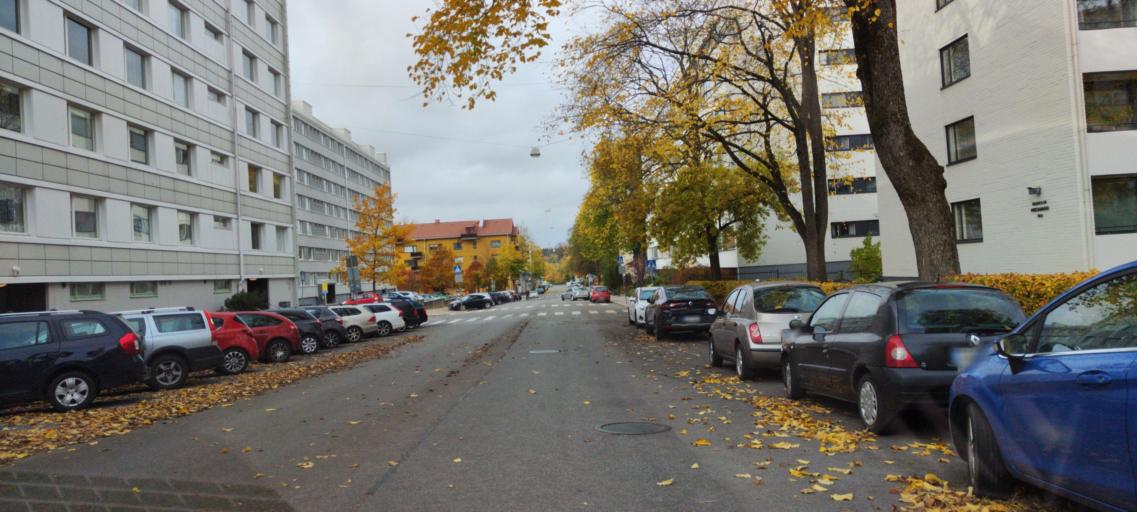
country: FI
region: Varsinais-Suomi
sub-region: Turku
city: Turku
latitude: 60.4466
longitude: 22.2496
